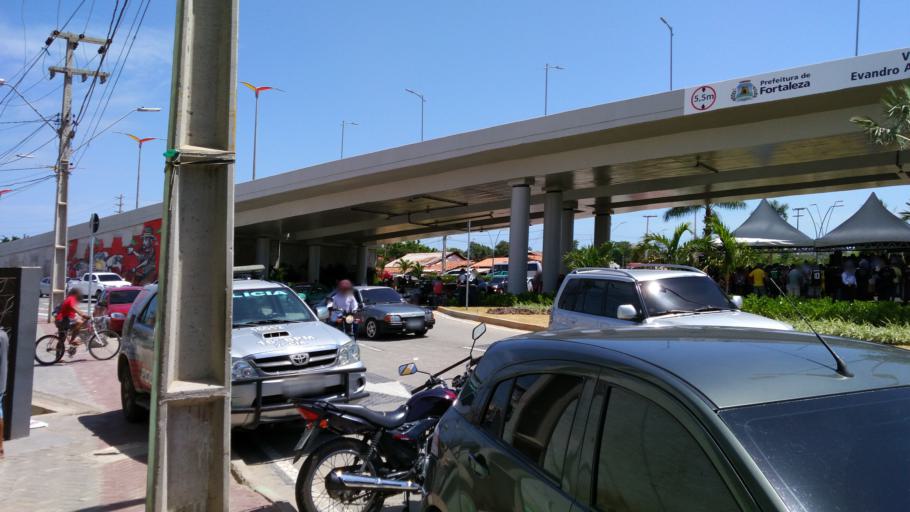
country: BR
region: Ceara
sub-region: Fortaleza
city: Fortaleza
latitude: -3.7638
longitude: -38.5090
